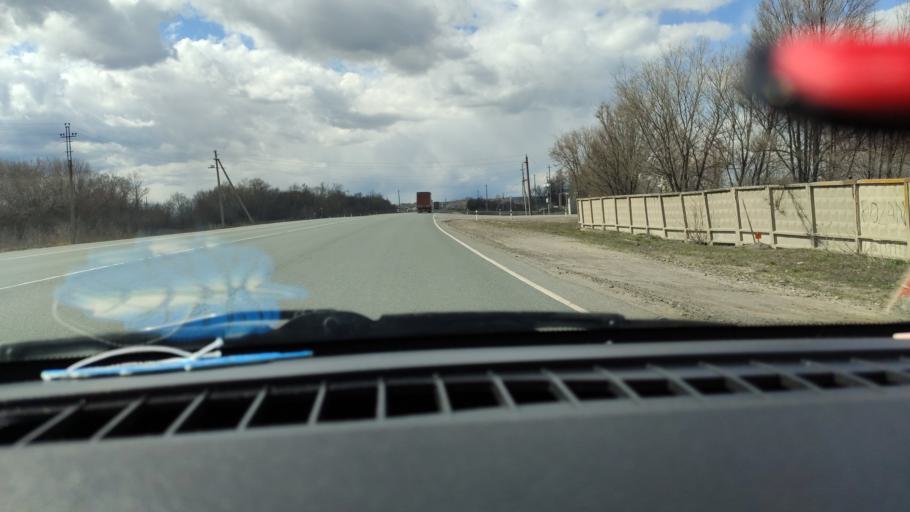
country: RU
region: Samara
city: Varlamovo
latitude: 53.1934
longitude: 48.3322
